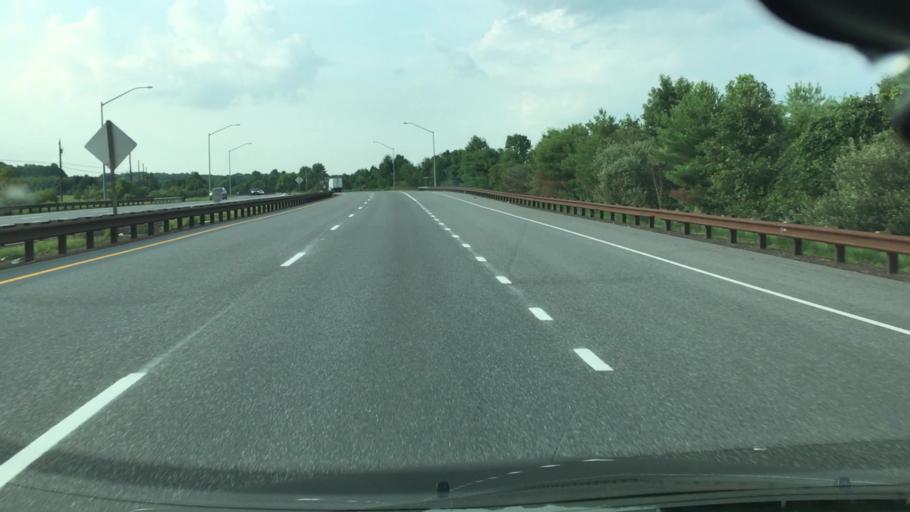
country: US
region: Delaware
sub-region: Sussex County
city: Selbyville
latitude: 38.4135
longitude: -75.2125
